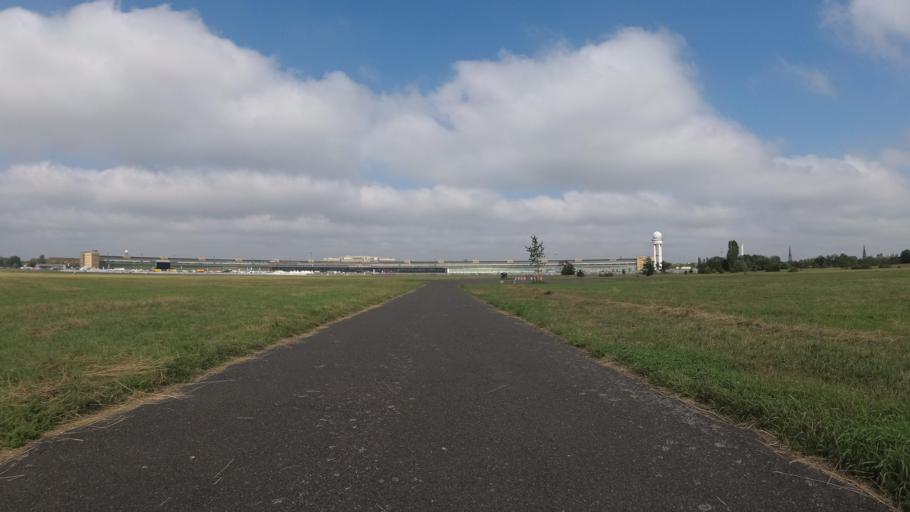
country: DE
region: Berlin
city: Tempelhof Bezirk
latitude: 52.4755
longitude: 13.3996
